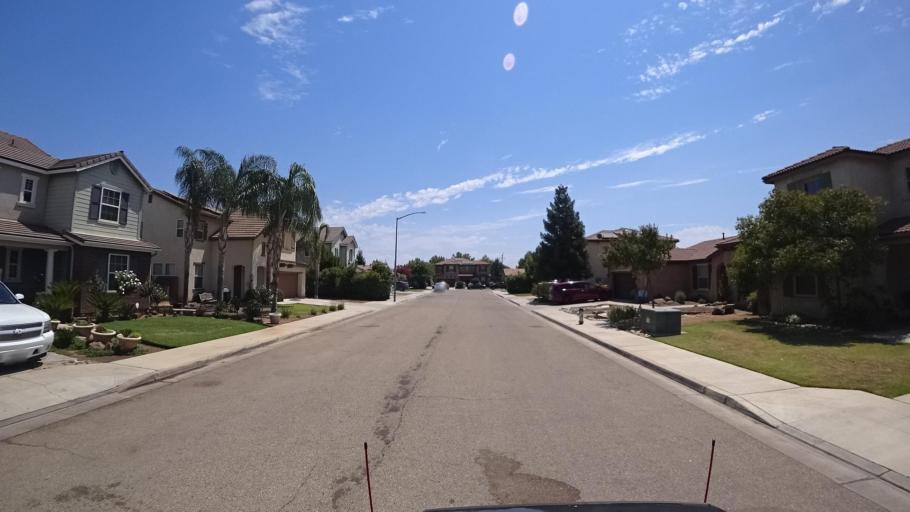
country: US
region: California
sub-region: Fresno County
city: Tarpey Village
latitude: 36.7840
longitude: -119.6567
